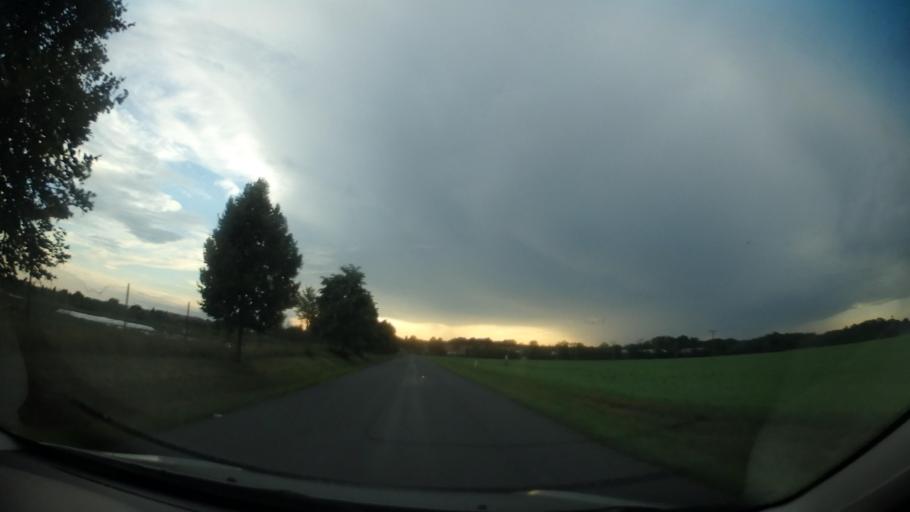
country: CZ
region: Zlin
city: Chropyne
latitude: 49.3874
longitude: 17.3586
